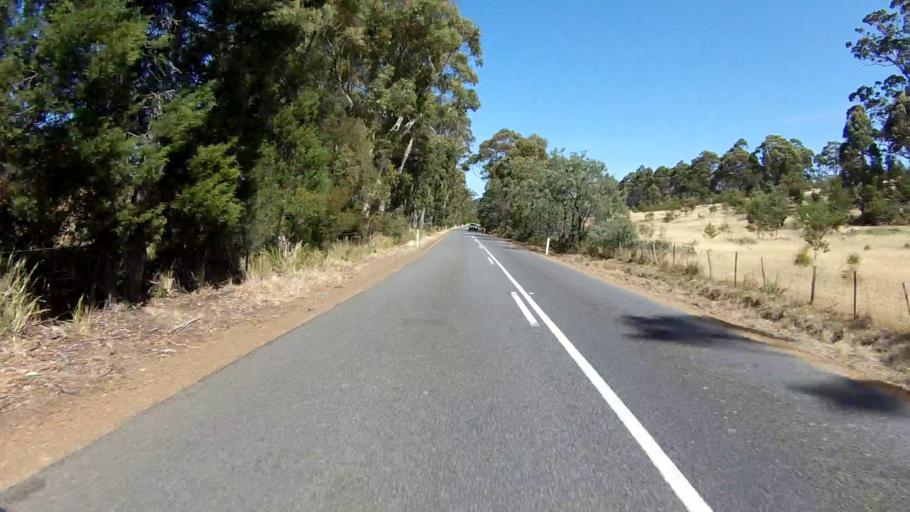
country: AU
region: Tasmania
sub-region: Sorell
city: Sorell
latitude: -42.3118
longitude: 147.9613
